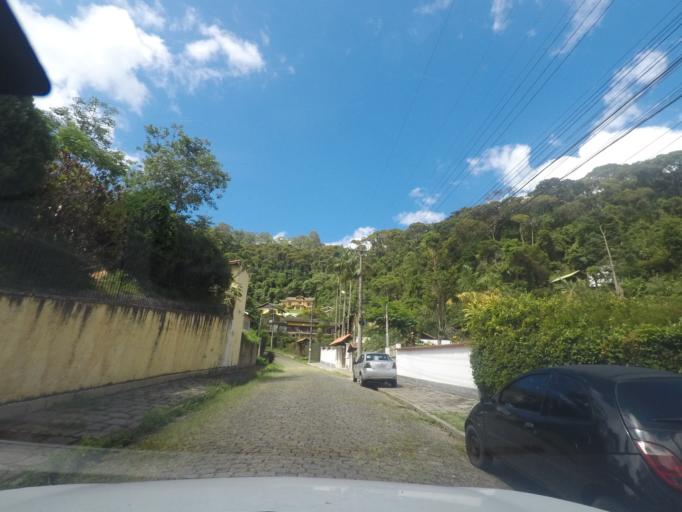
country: BR
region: Rio de Janeiro
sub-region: Teresopolis
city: Teresopolis
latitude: -22.3968
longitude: -42.9873
